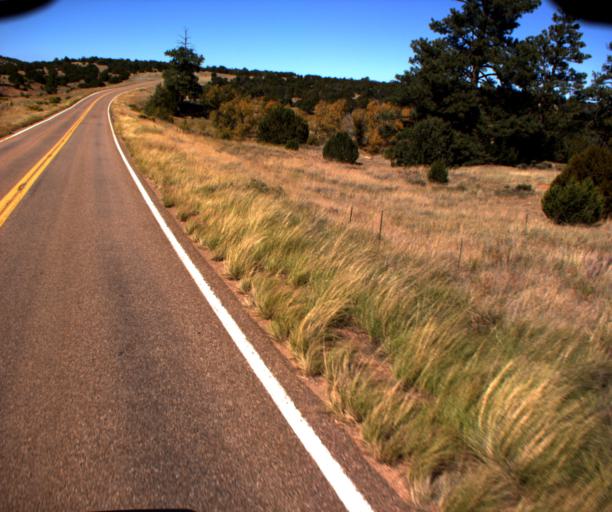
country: US
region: Arizona
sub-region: Navajo County
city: Heber-Overgaard
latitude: 34.4529
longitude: -110.4577
